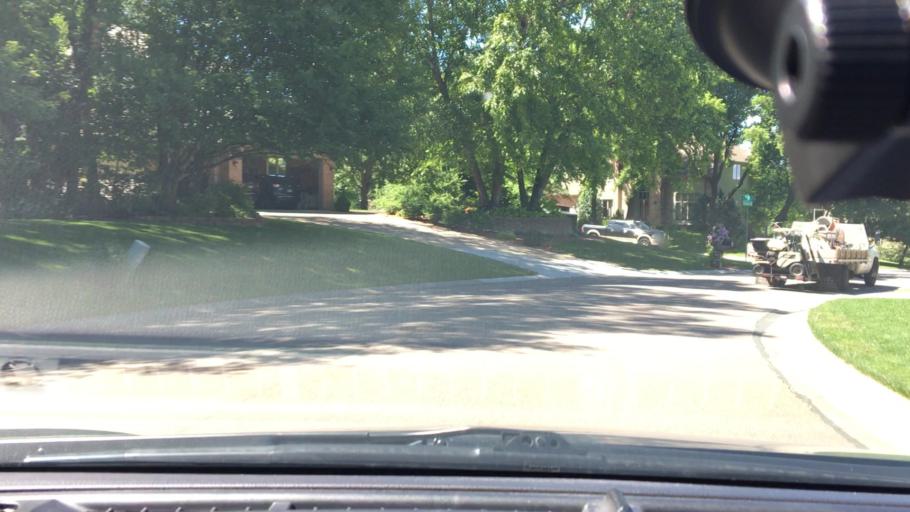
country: US
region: Minnesota
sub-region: Hennepin County
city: Maple Grove
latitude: 45.0698
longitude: -93.4627
